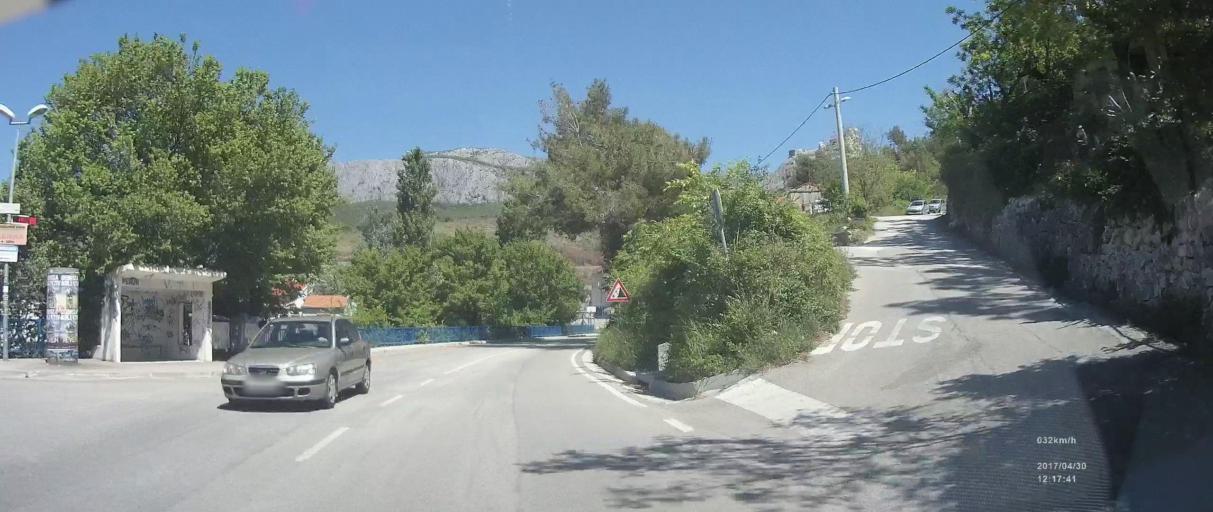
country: HR
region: Splitsko-Dalmatinska
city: Zrnovnica
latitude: 43.5159
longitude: 16.5424
